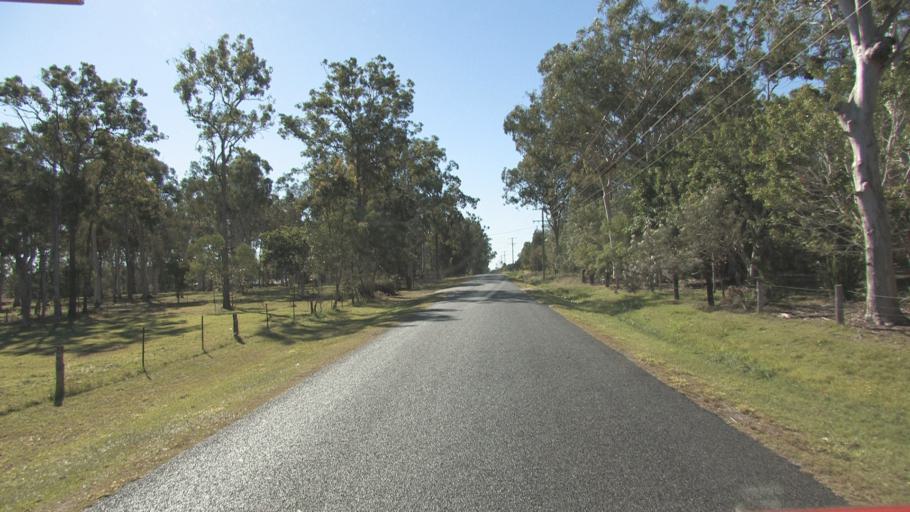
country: AU
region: Queensland
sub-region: Logan
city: Logan Reserve
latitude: -27.7284
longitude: 153.0727
